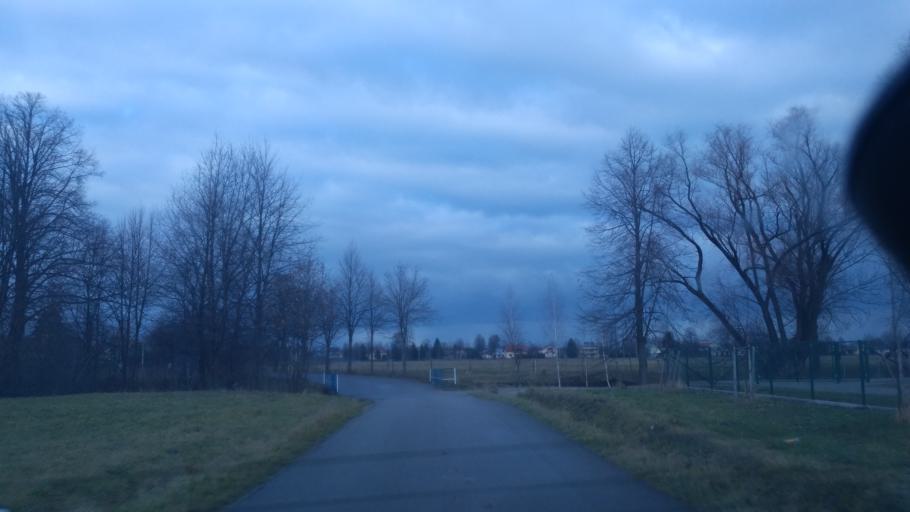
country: PL
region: Subcarpathian Voivodeship
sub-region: Powiat lancucki
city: Czarna
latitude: 50.0943
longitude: 22.1804
